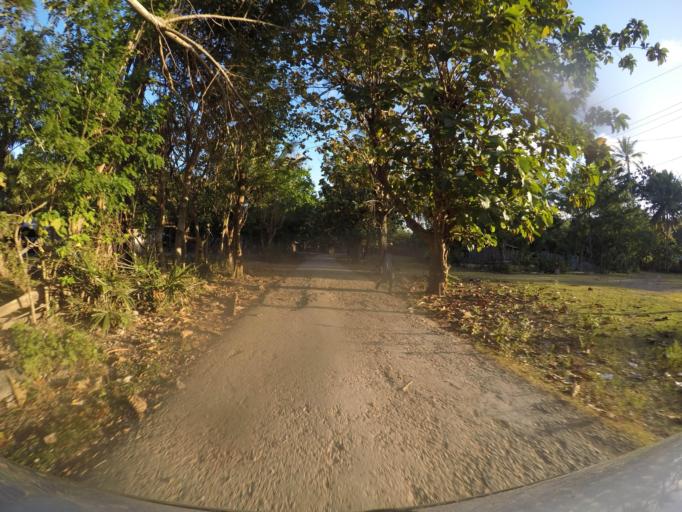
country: TL
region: Baucau
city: Venilale
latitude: -8.7388
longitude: 126.7147
